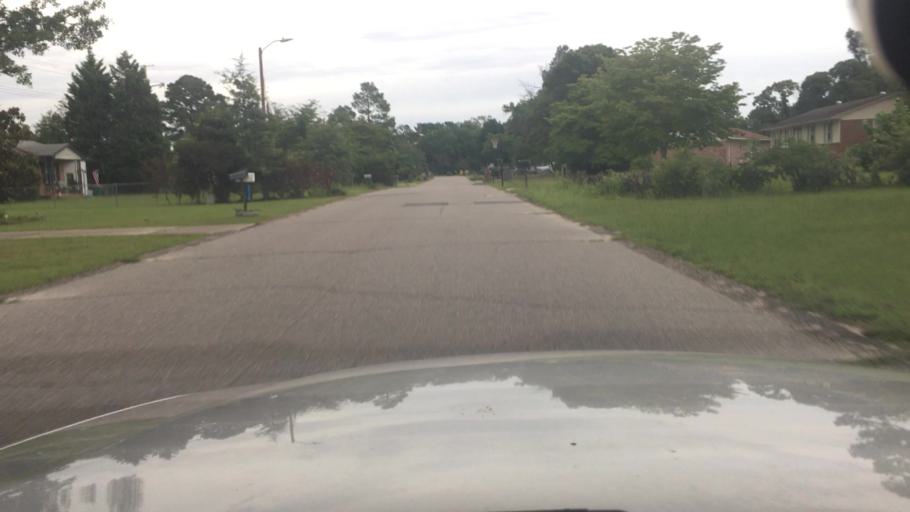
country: US
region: North Carolina
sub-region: Cumberland County
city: Hope Mills
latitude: 34.9691
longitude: -78.9747
